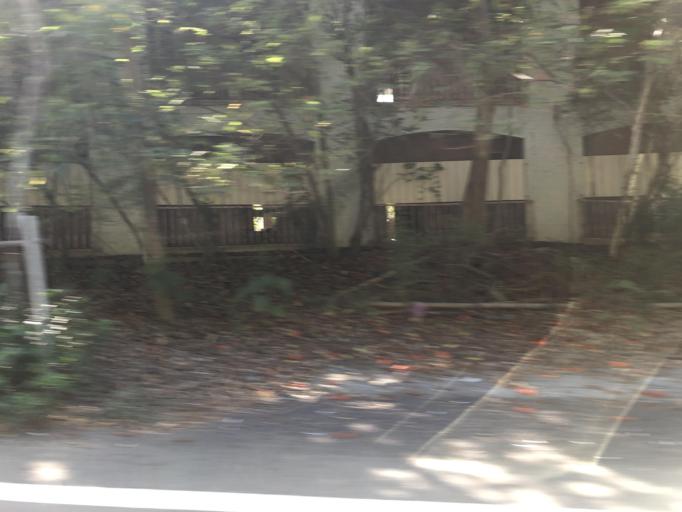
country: TW
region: Taiwan
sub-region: Tainan
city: Tainan
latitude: 23.0372
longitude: 120.3400
